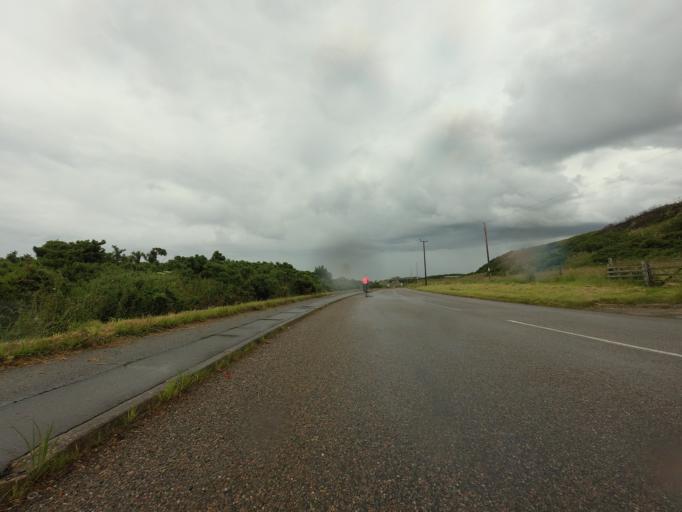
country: GB
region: Scotland
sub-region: Moray
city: Buckie
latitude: 57.6713
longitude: -2.9945
